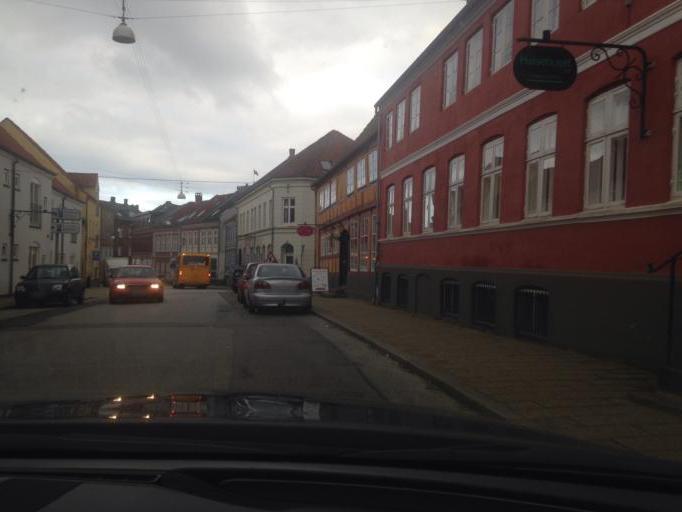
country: DK
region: South Denmark
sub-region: Kolding Kommune
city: Kolding
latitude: 55.4931
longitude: 9.4680
